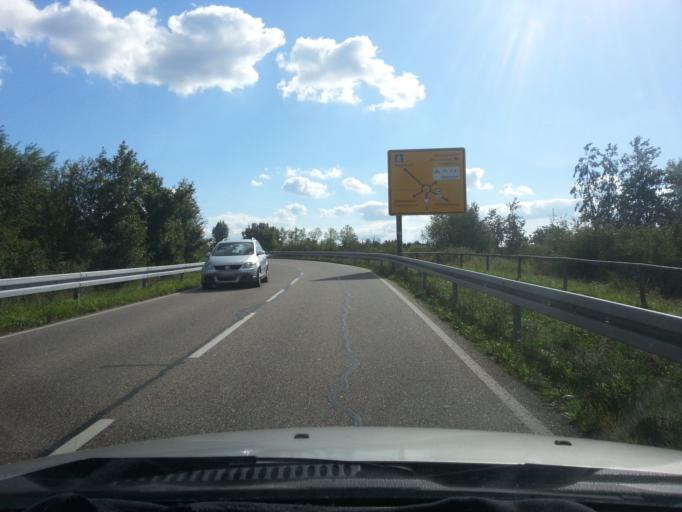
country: DE
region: Baden-Wuerttemberg
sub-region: Karlsruhe Region
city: Philippsburg
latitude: 49.2433
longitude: 8.4722
